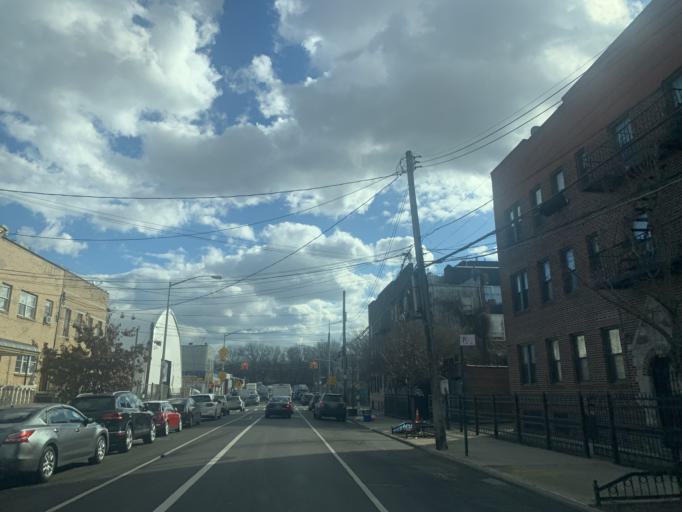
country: US
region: New York
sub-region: Kings County
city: East New York
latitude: 40.6929
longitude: -73.9035
